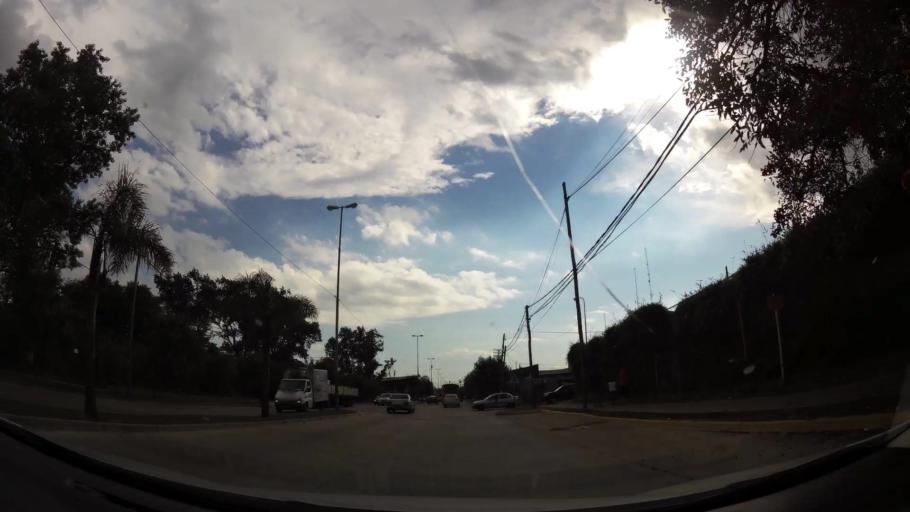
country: AR
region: Buenos Aires
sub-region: Partido de Tigre
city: Tigre
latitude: -34.4824
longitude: -58.6094
